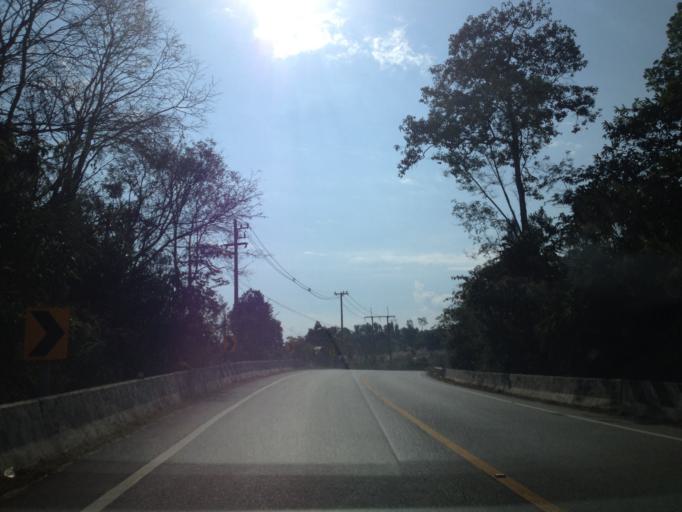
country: TH
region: Mae Hong Son
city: Pa Pae
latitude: 18.1652
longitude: 98.2321
